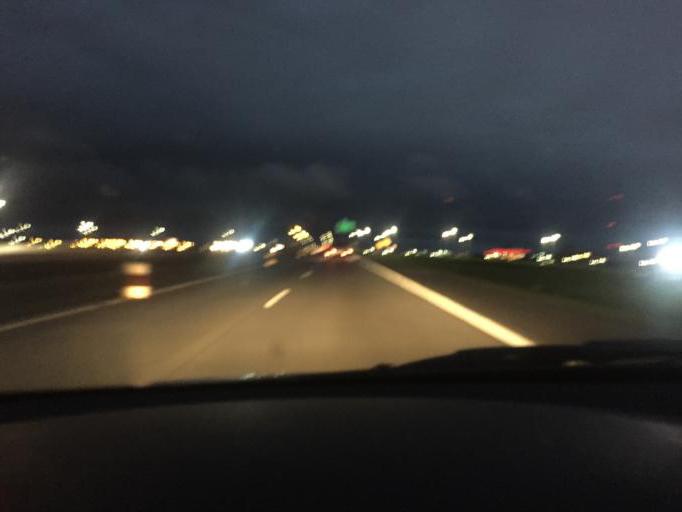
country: AR
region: Cordoba
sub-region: Departamento de Capital
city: Cordoba
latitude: -31.3548
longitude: -64.2061
